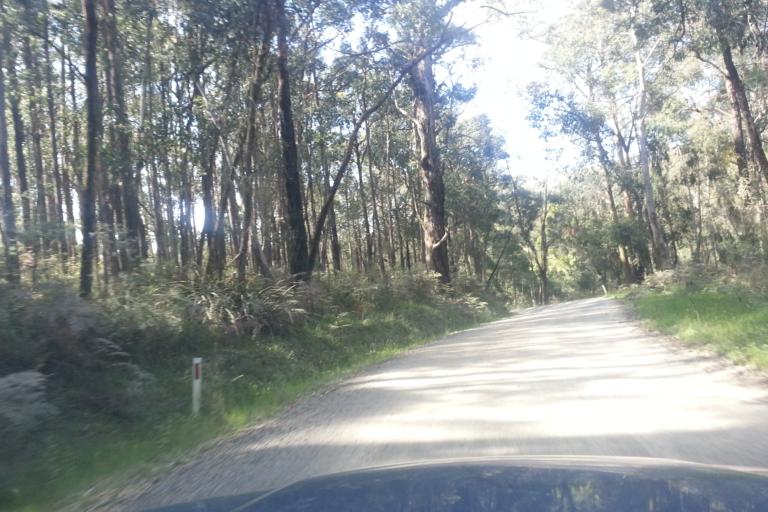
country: AU
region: Victoria
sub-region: Cardinia
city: Cockatoo
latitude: -37.9786
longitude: 145.4728
